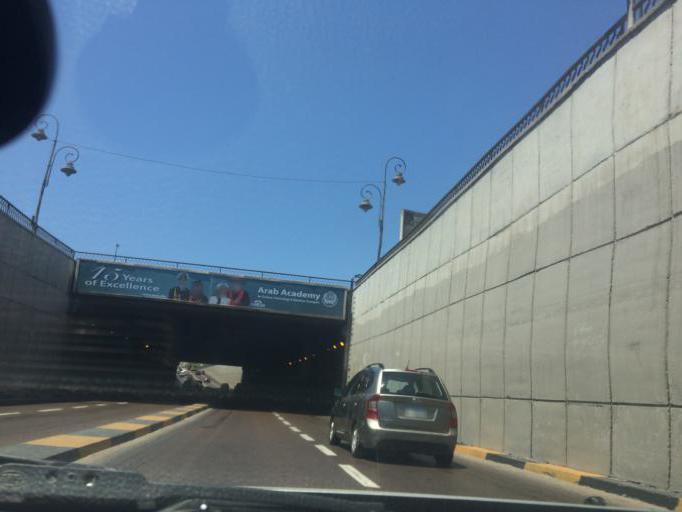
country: EG
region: Alexandria
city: Alexandria
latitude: 31.2008
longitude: 29.9162
